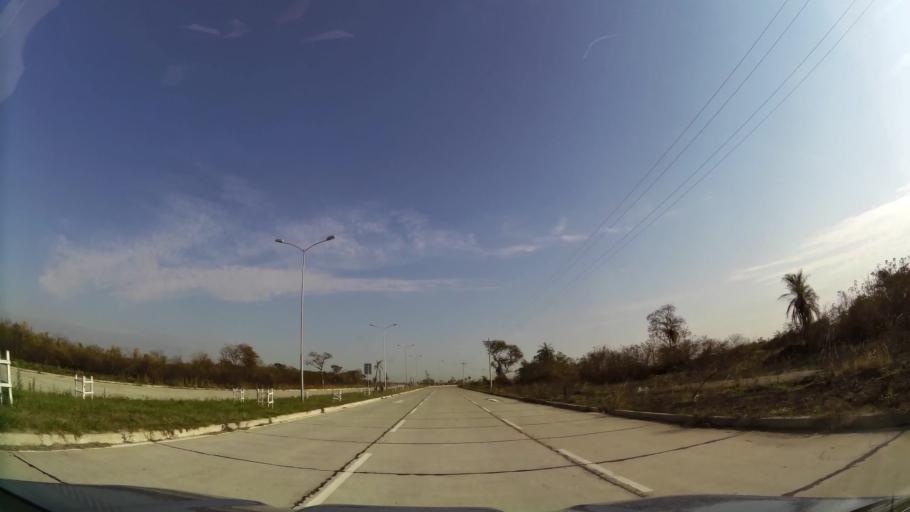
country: BO
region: Santa Cruz
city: Santa Cruz de la Sierra
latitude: -17.6710
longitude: -63.1276
